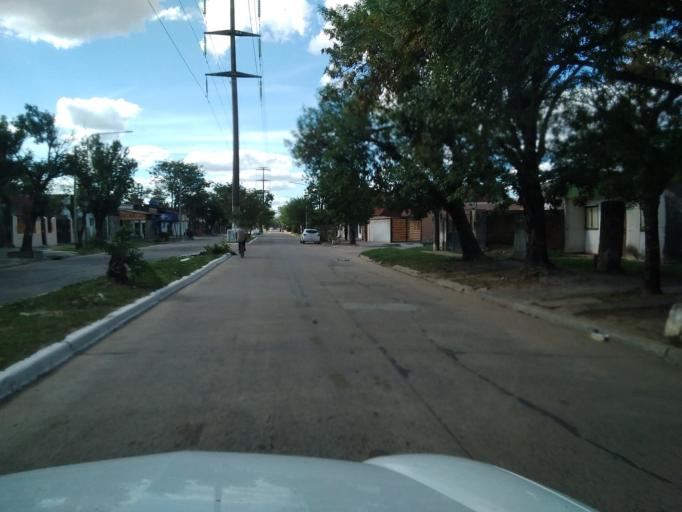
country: AR
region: Corrientes
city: Corrientes
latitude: -27.4963
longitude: -58.8381
